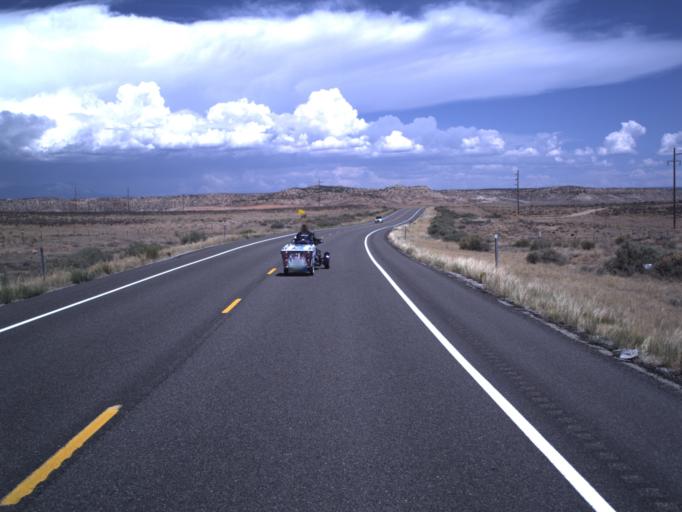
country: US
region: Utah
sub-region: San Juan County
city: Blanding
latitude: 37.3943
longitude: -109.4977
